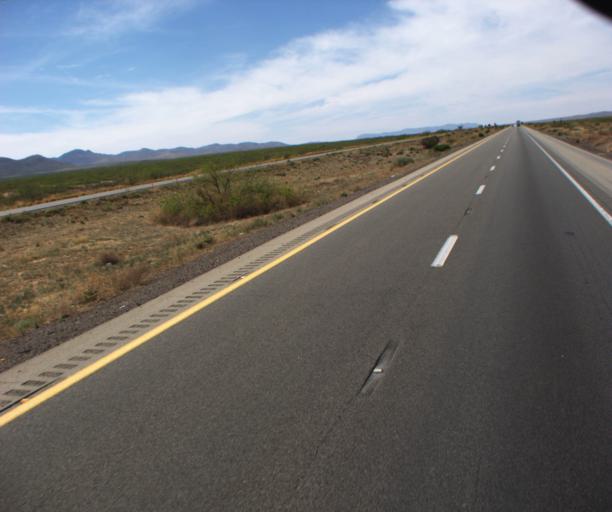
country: US
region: Arizona
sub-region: Cochise County
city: Willcox
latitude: 32.3376
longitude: -109.5460
